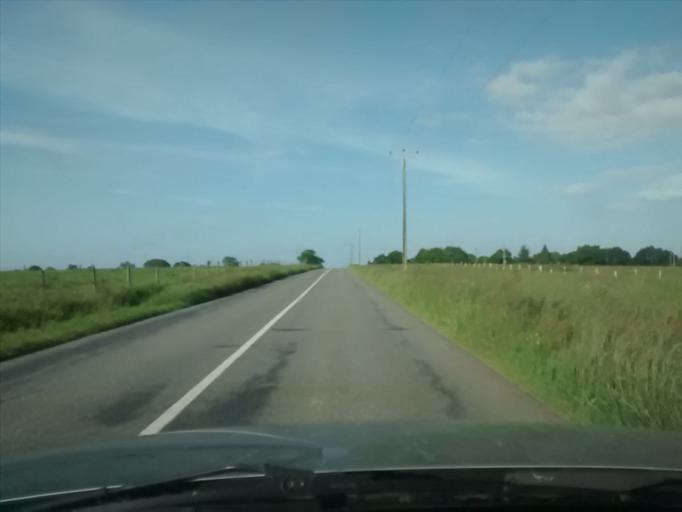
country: FR
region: Pays de la Loire
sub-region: Departement de la Mayenne
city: Meslay-du-Maine
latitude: 47.9402
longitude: -0.6431
